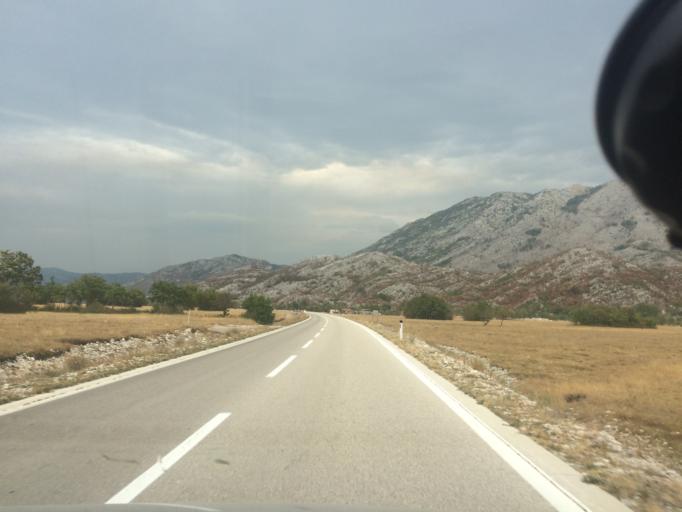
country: ME
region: Kotor
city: Risan
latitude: 42.5929
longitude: 18.6897
